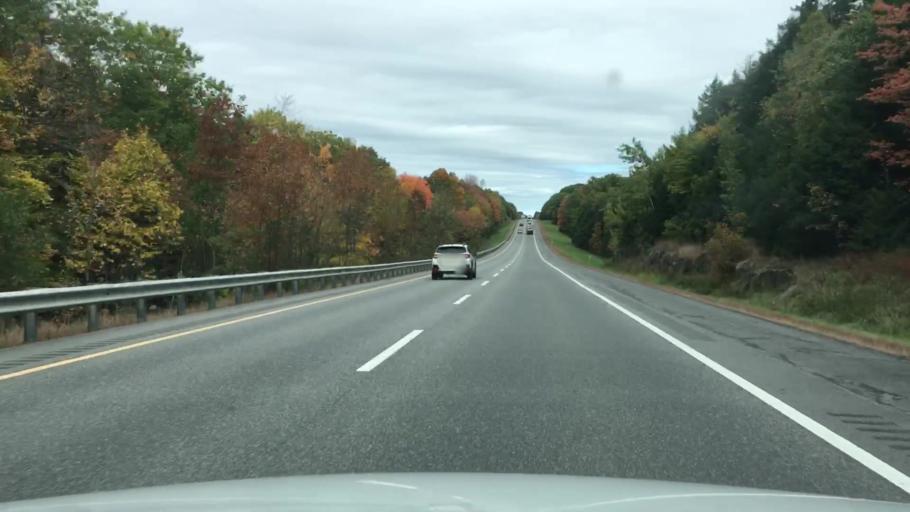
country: US
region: Maine
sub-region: Kennebec County
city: Sidney
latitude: 44.3990
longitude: -69.7532
